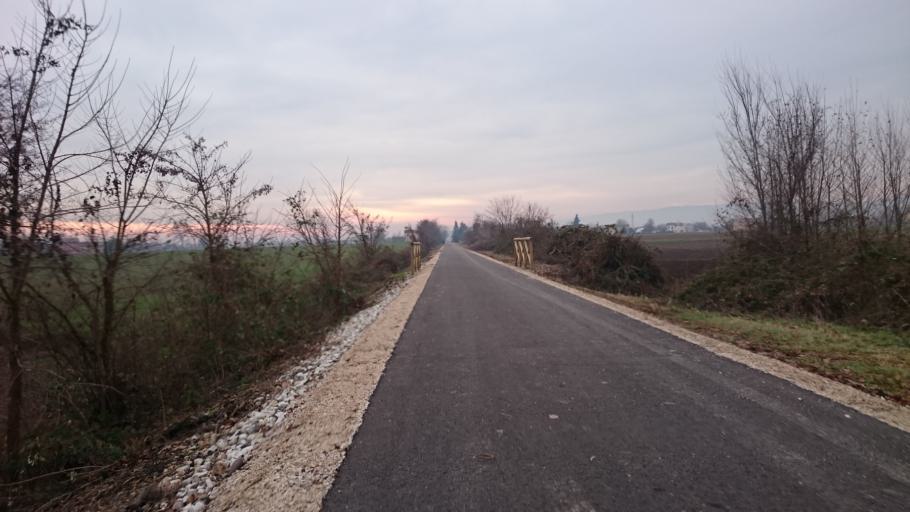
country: IT
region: Veneto
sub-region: Provincia di Vicenza
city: Montegalda
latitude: 45.4794
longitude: 11.6750
